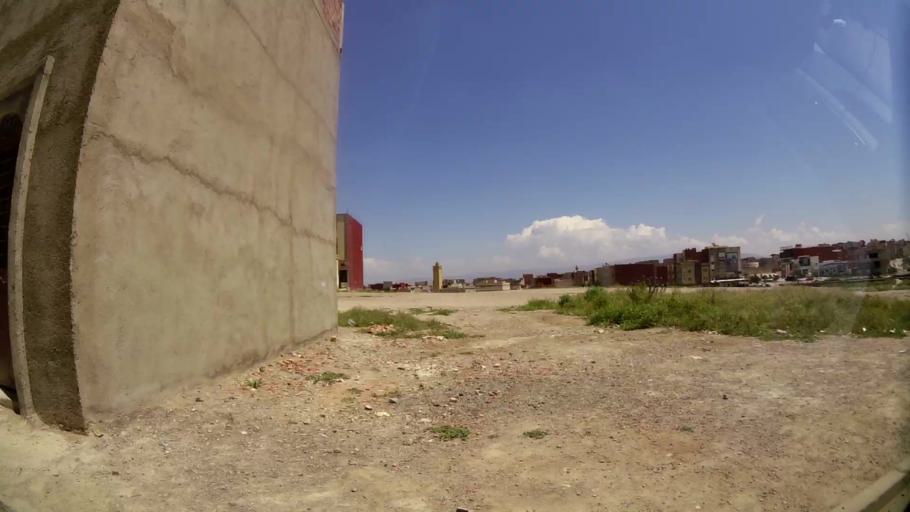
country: MA
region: Oriental
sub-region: Oujda-Angad
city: Oujda
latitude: 34.6857
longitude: -1.9527
